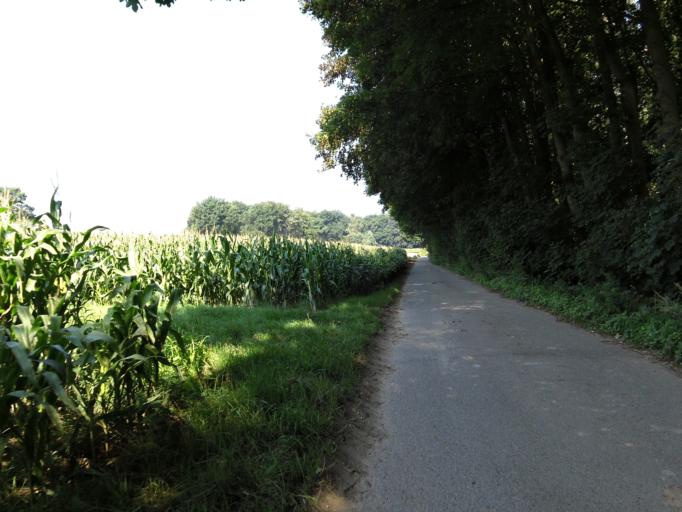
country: DE
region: North Rhine-Westphalia
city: Huckelhoven
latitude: 51.0181
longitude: 6.2084
